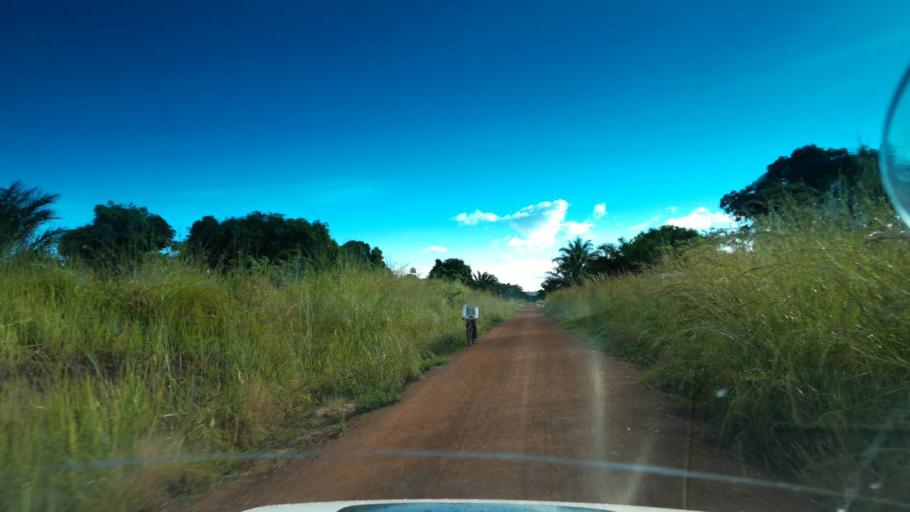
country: ZM
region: Northern
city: Kaputa
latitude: -8.3970
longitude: 28.9425
